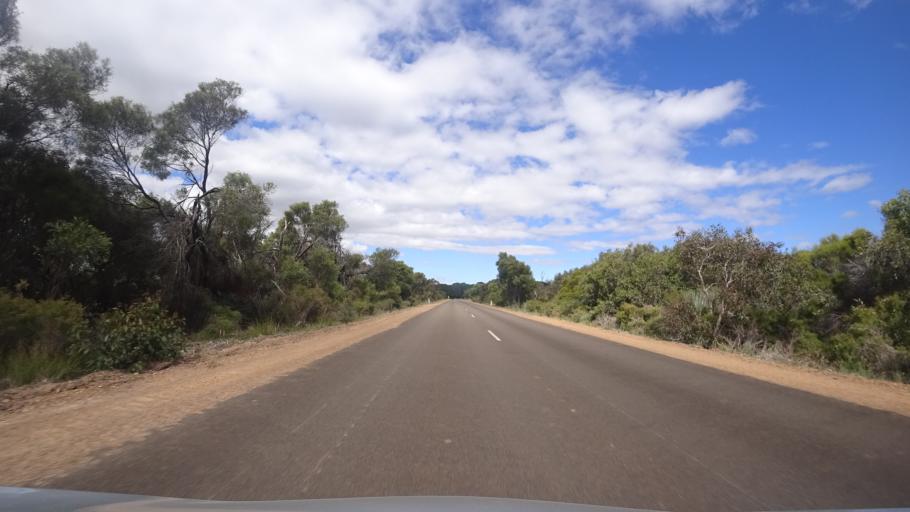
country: AU
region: South Australia
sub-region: Kangaroo Island
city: Kingscote
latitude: -35.7957
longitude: 137.0300
